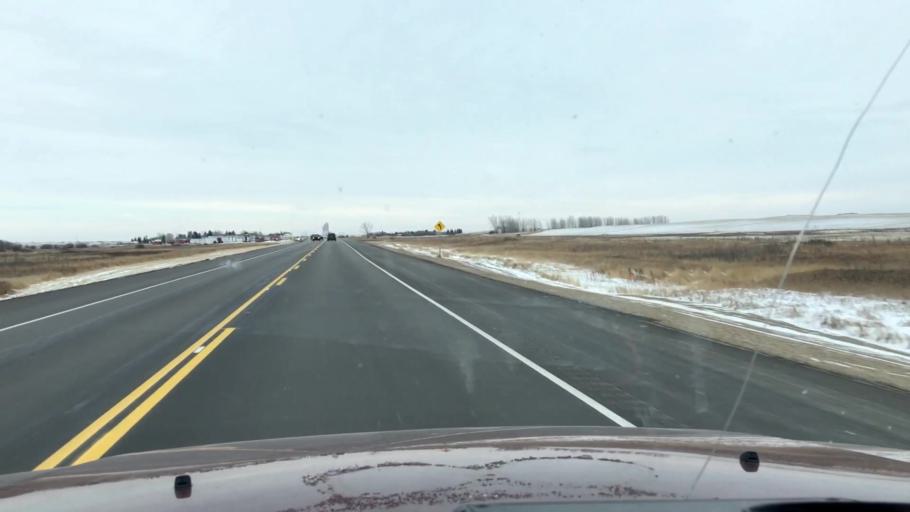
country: CA
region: Saskatchewan
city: Moose Jaw
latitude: 50.8588
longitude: -105.5844
